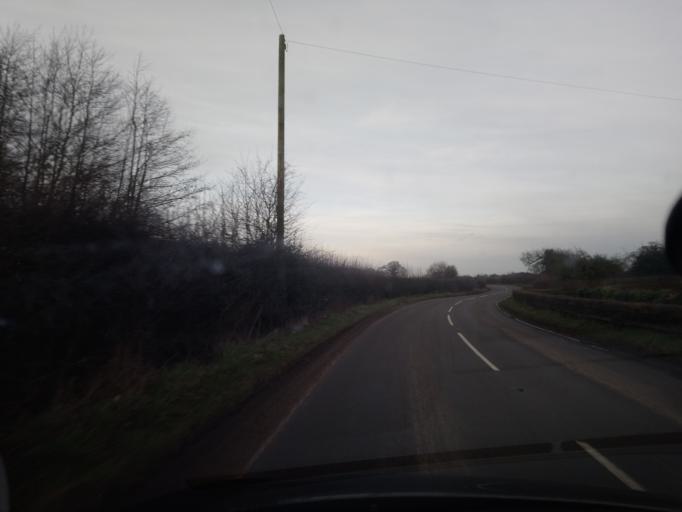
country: GB
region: England
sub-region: Shropshire
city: Whitchurch
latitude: 52.9400
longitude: -2.6822
